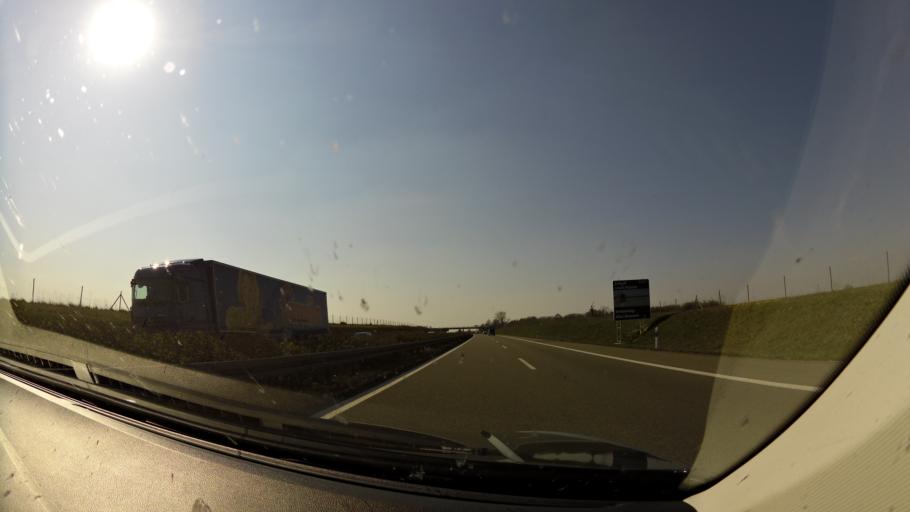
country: DE
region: Mecklenburg-Vorpommern
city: Grimmen
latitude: 54.0901
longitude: 13.1085
